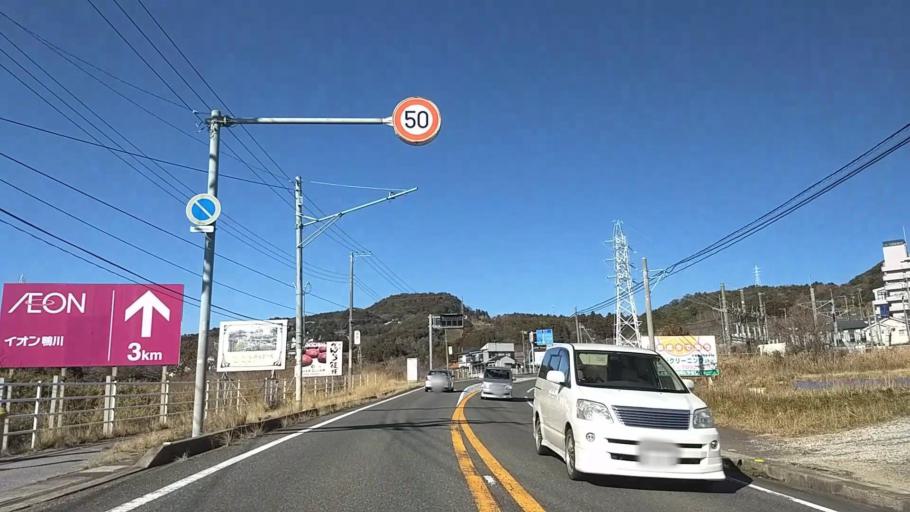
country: JP
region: Chiba
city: Kawaguchi
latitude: 35.0883
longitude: 140.0907
